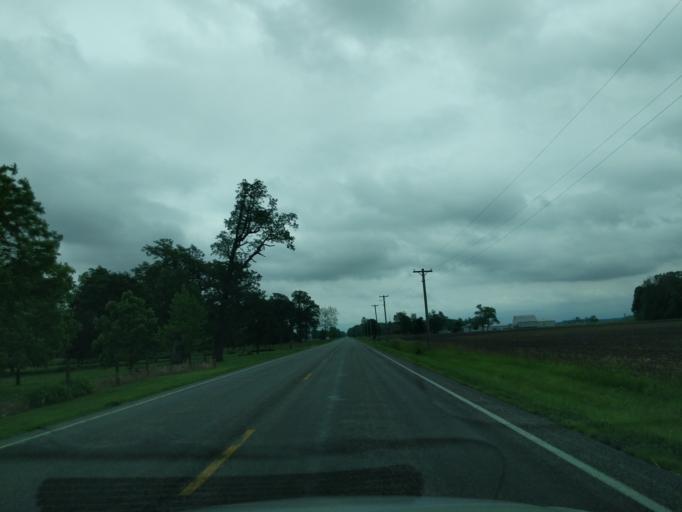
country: US
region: Indiana
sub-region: Tipton County
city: Tipton
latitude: 40.2833
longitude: -85.9809
